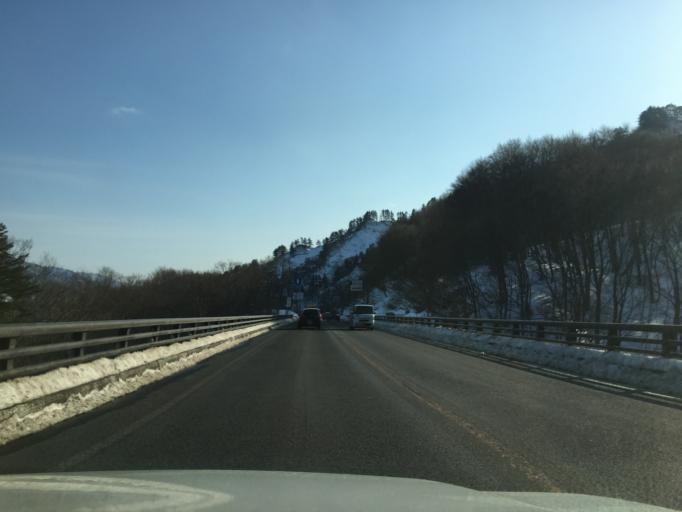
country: JP
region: Yamagata
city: Sagae
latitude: 38.4632
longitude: 139.9917
